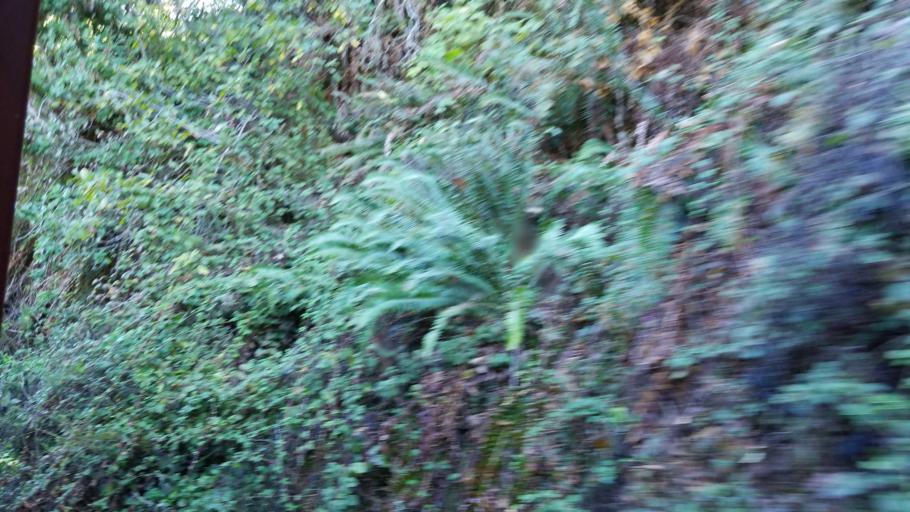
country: US
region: California
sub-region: Mendocino County
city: Fort Bragg
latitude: 39.4473
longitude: -123.7872
